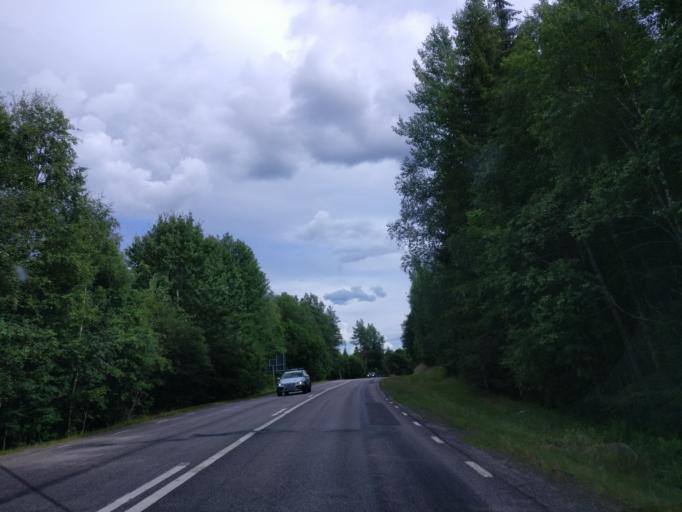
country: SE
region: Vaermland
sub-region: Hagfors Kommun
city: Ekshaerad
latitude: 60.1583
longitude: 13.5124
